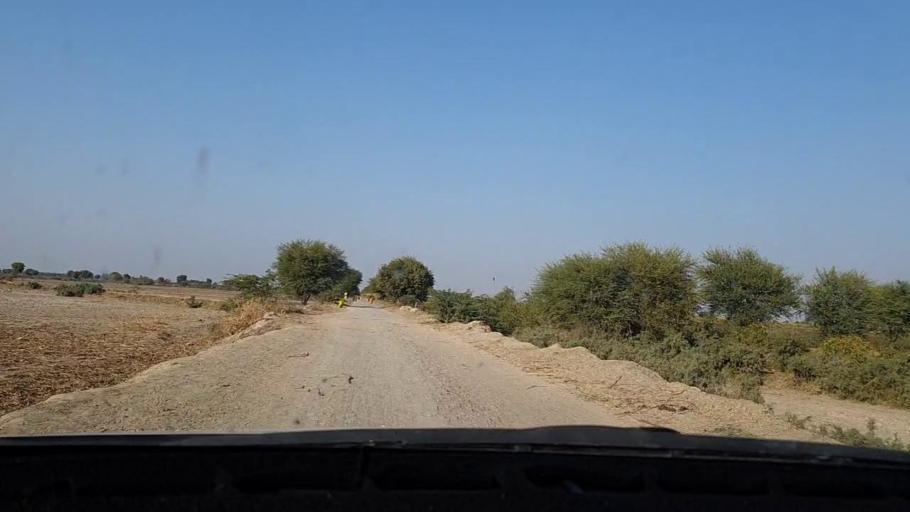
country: PK
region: Sindh
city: Tando Mittha Khan
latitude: 25.8464
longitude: 69.3327
